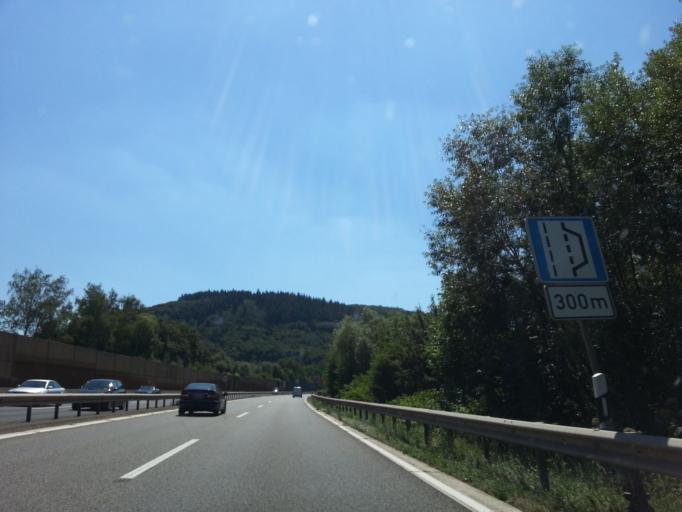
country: DE
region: Rheinland-Pfalz
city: Kenn
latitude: 49.7876
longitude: 6.7060
